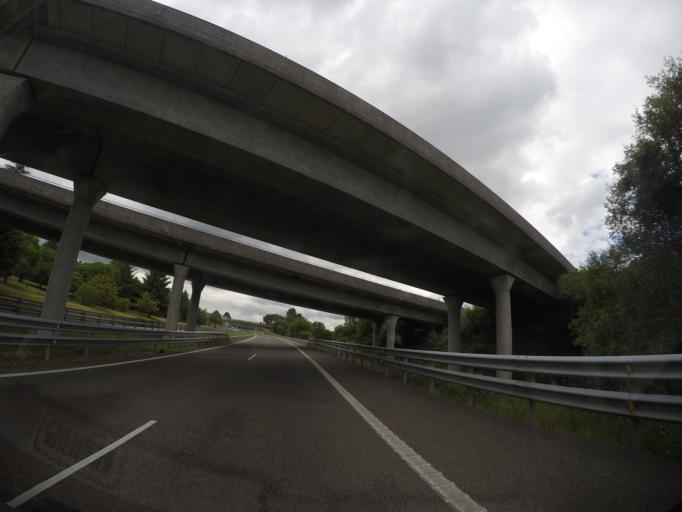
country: ES
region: Galicia
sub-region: Provincia da Coruna
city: Betanzos
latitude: 43.2619
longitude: -8.2545
